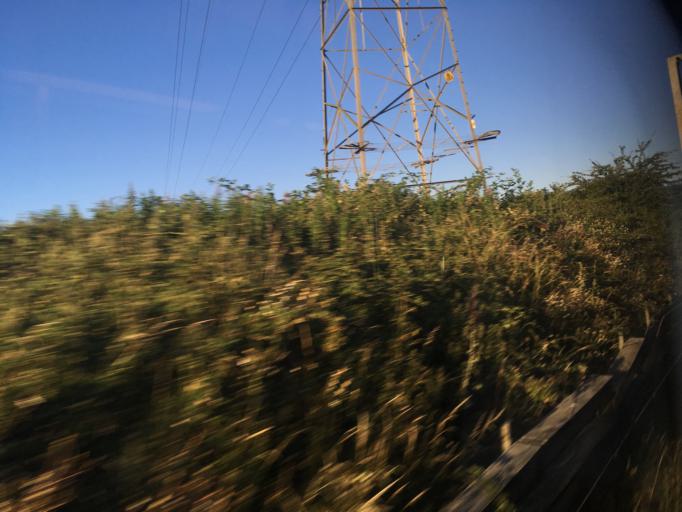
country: GB
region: England
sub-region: Hertfordshire
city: Bovingdon
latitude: 51.7531
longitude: -0.5355
